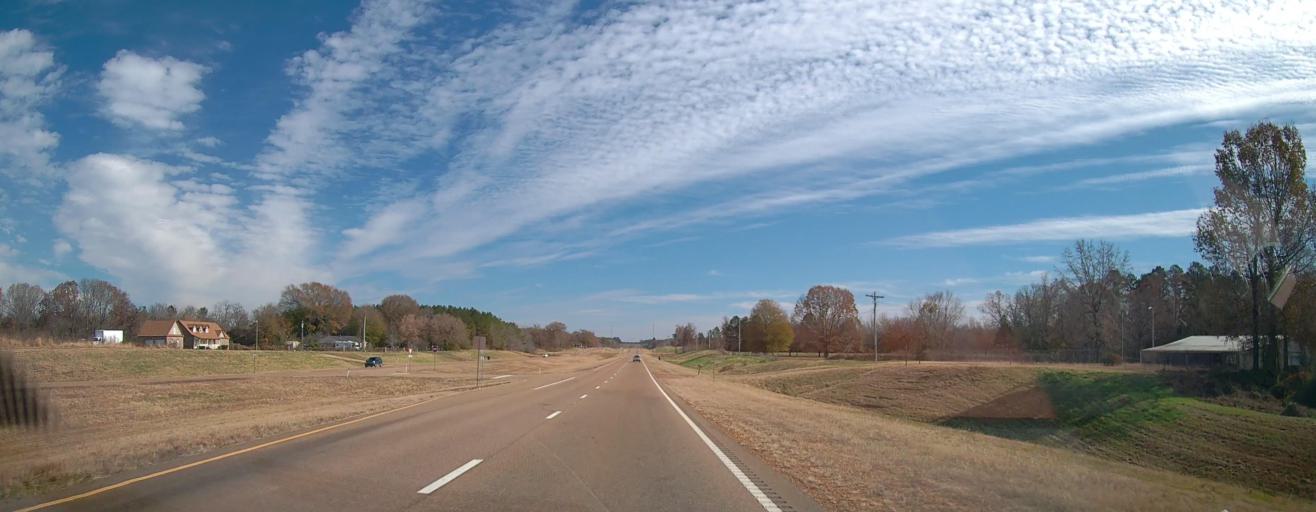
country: US
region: Mississippi
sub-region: Benton County
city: Ashland
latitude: 34.9458
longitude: -89.1784
